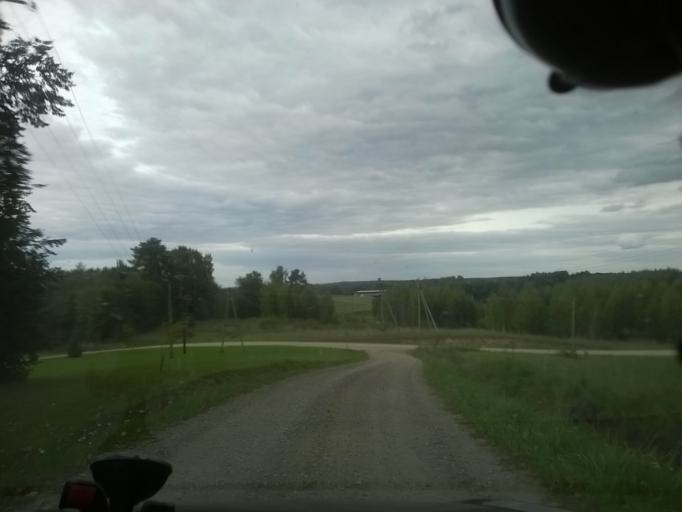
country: EE
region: Vorumaa
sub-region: Voru linn
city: Voru
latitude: 57.8104
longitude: 27.1678
